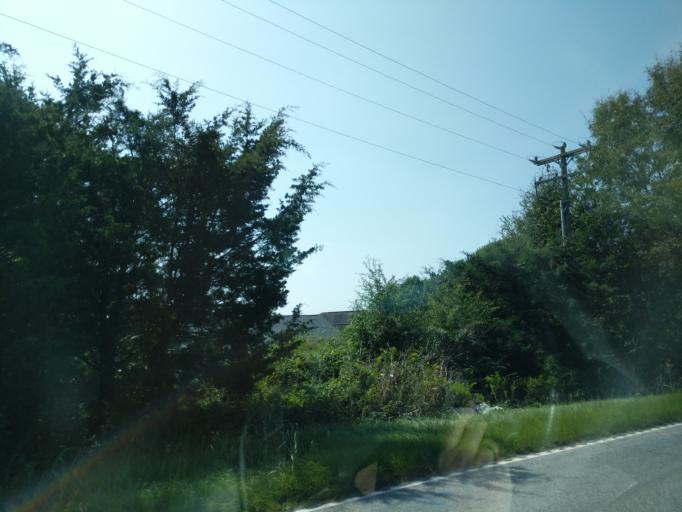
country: US
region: South Carolina
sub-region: Spartanburg County
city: Duncan
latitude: 34.8956
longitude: -82.1304
